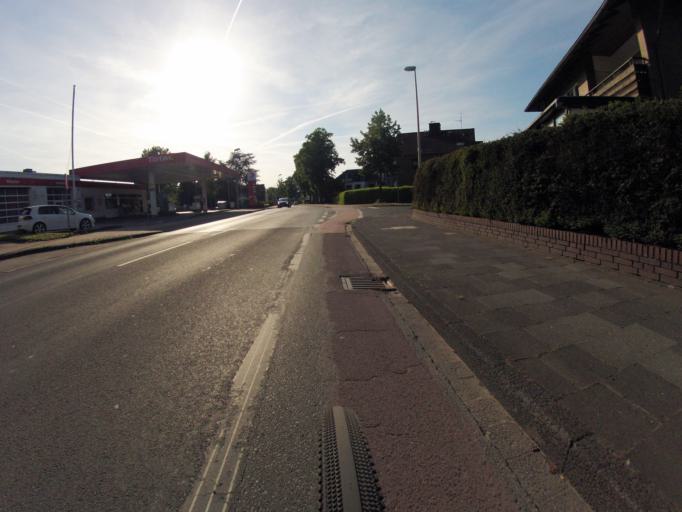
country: DE
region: North Rhine-Westphalia
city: Ibbenburen
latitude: 52.2746
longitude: 7.7053
